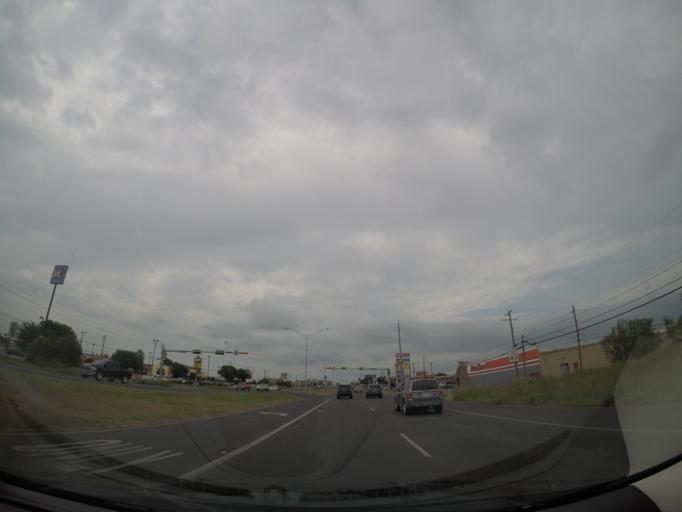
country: US
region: Texas
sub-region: Val Verde County
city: Del Rio
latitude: 29.3940
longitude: -100.9052
